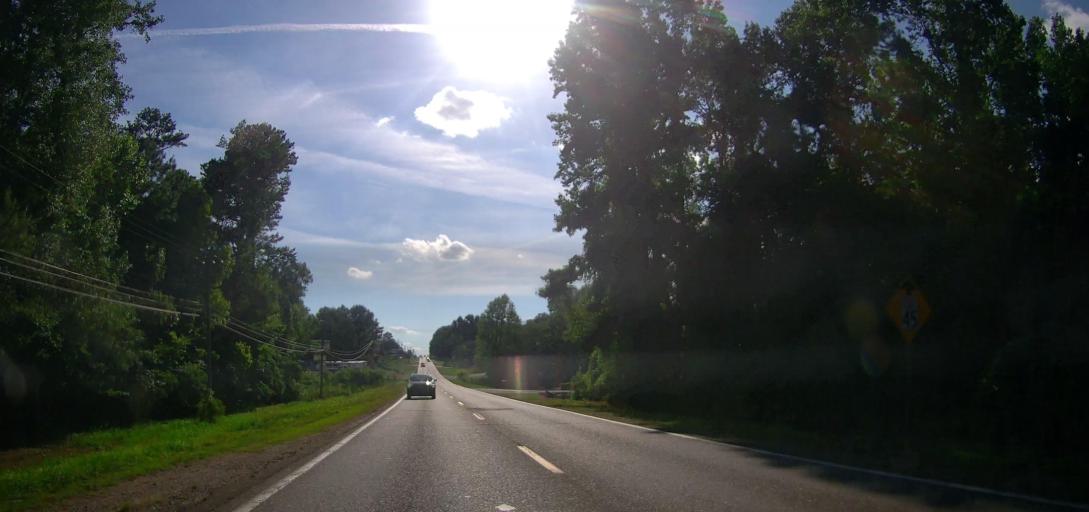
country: US
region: Alabama
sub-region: Tuscaloosa County
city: Holt
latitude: 33.1905
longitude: -87.4383
